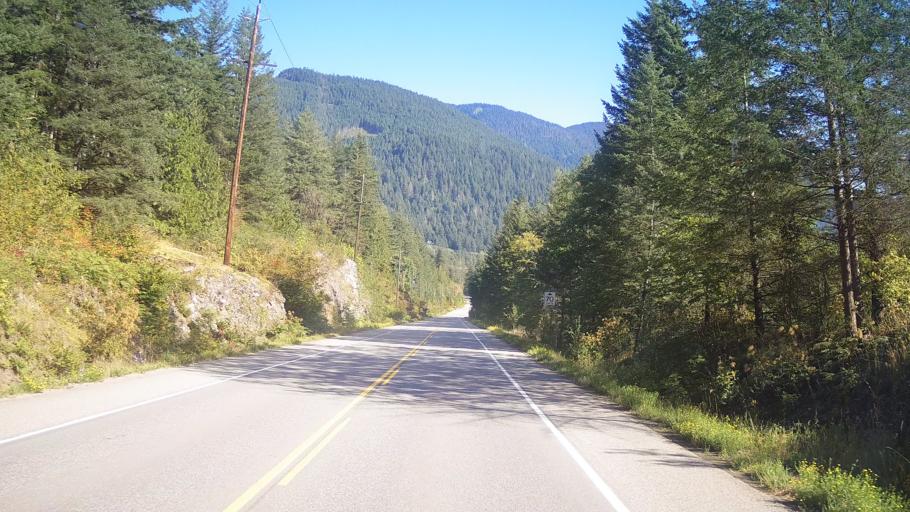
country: CA
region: British Columbia
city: Hope
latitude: 49.5434
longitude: -121.4383
